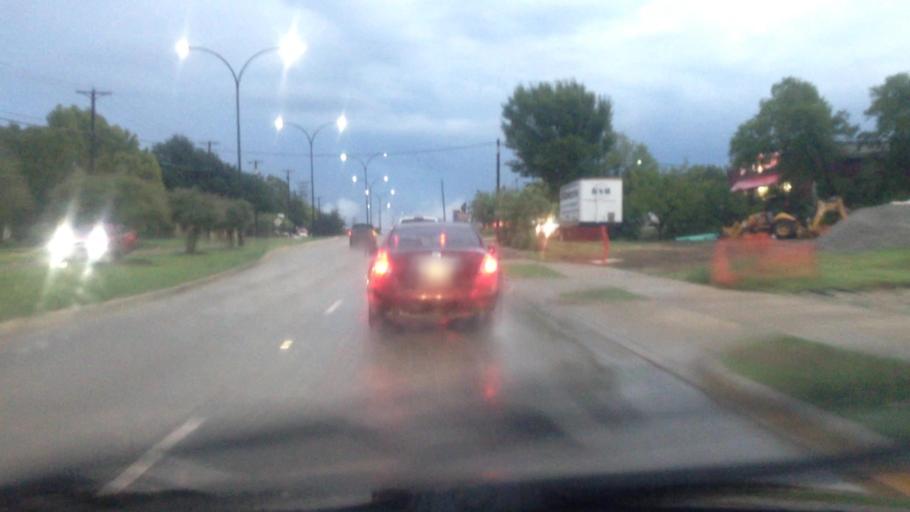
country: US
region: Texas
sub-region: Tarrant County
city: Arlington
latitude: 32.7353
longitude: -97.0789
